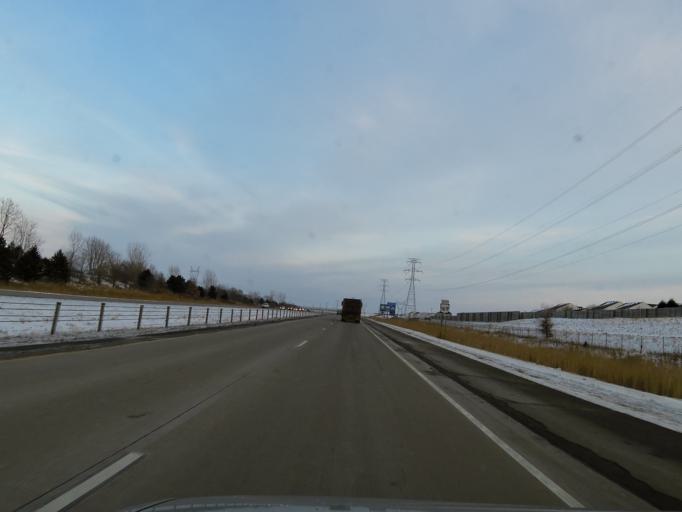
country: US
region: Minnesota
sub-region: Scott County
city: Shakopee
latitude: 44.7760
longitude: -93.5297
